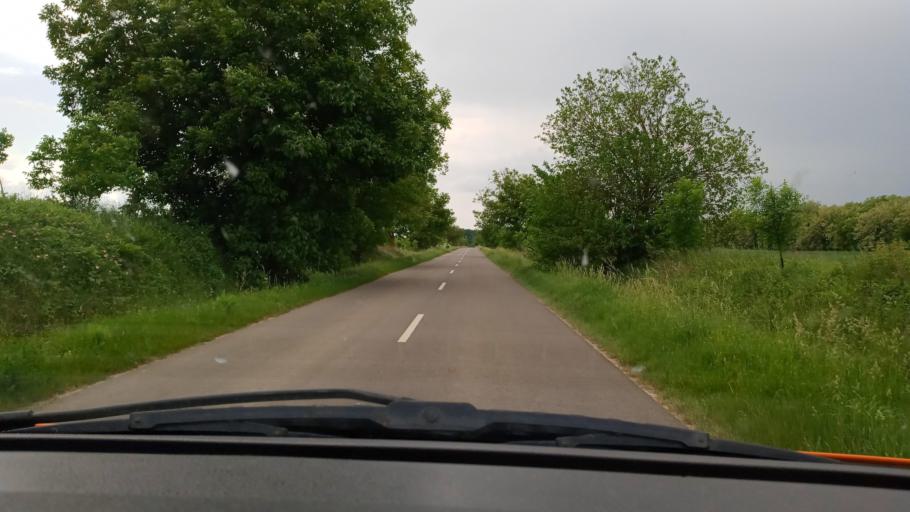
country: HU
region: Baranya
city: Vajszlo
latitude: 45.8525
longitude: 17.9816
